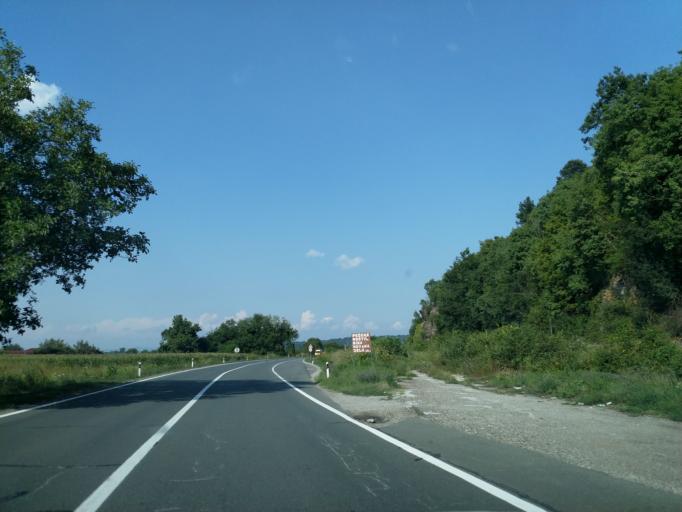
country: RS
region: Central Serbia
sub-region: Rasinski Okrug
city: Varvarin
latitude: 43.6698
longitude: 21.3967
